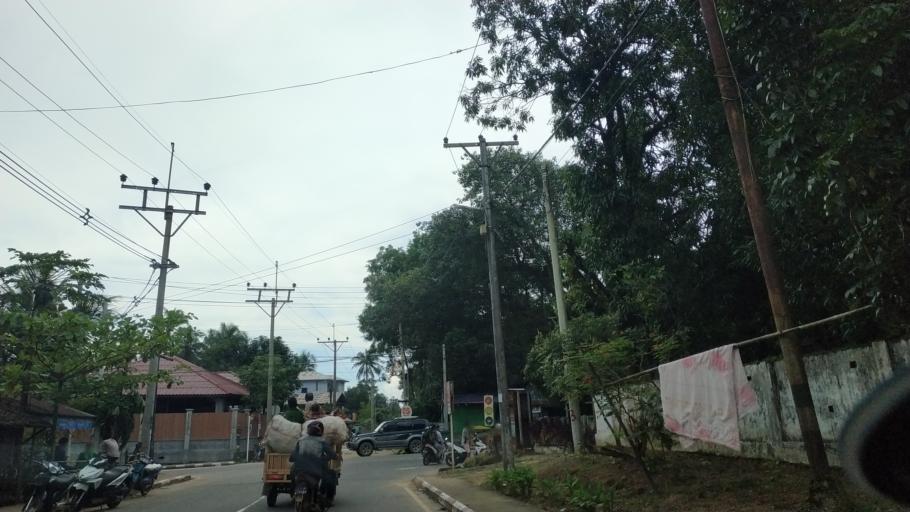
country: MM
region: Tanintharyi
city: Dawei
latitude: 14.0753
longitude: 98.2076
